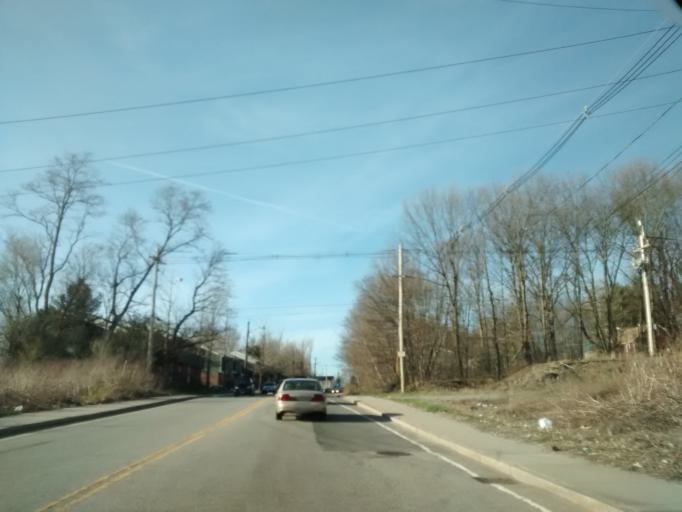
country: US
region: Massachusetts
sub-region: Worcester County
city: Sunderland
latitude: 42.2379
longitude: -71.7921
